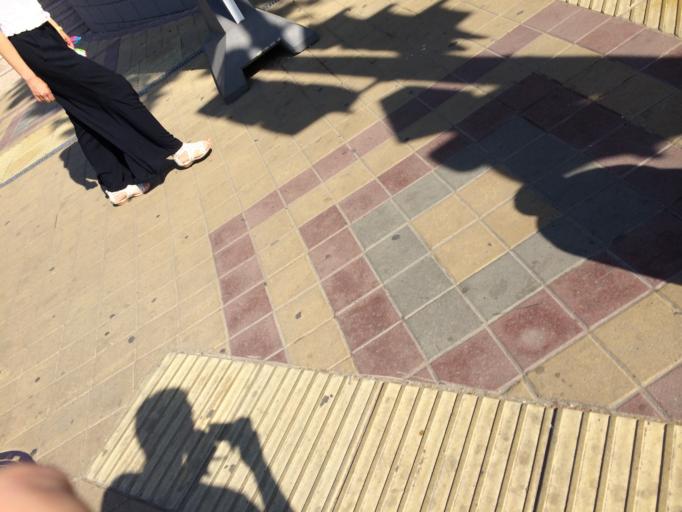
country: RU
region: Krasnodarskiy
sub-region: Sochi City
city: Sochi
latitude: 43.5931
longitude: 39.7278
